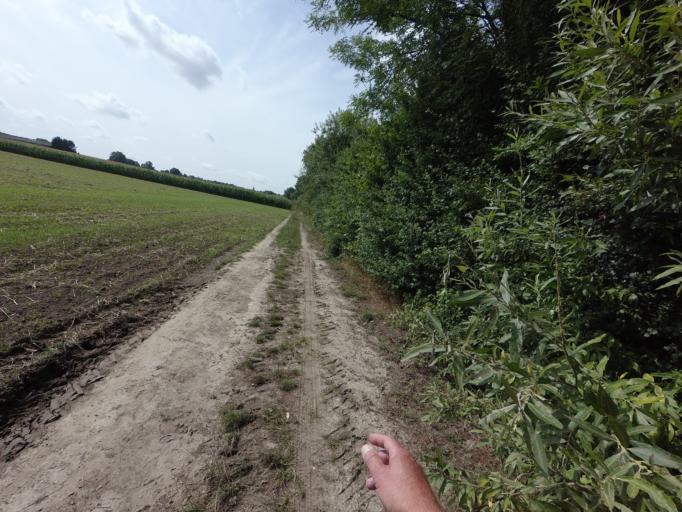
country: DE
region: North Rhine-Westphalia
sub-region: Regierungsbezirk Koln
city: Ubach-Palenberg
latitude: 50.9310
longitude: 6.0601
